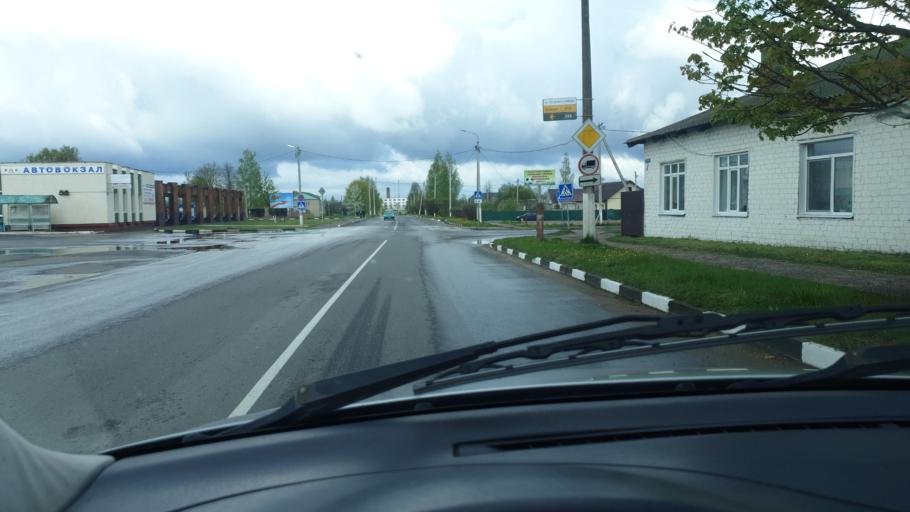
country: BY
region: Vitebsk
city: Lyepyel'
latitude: 54.8766
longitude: 28.6907
